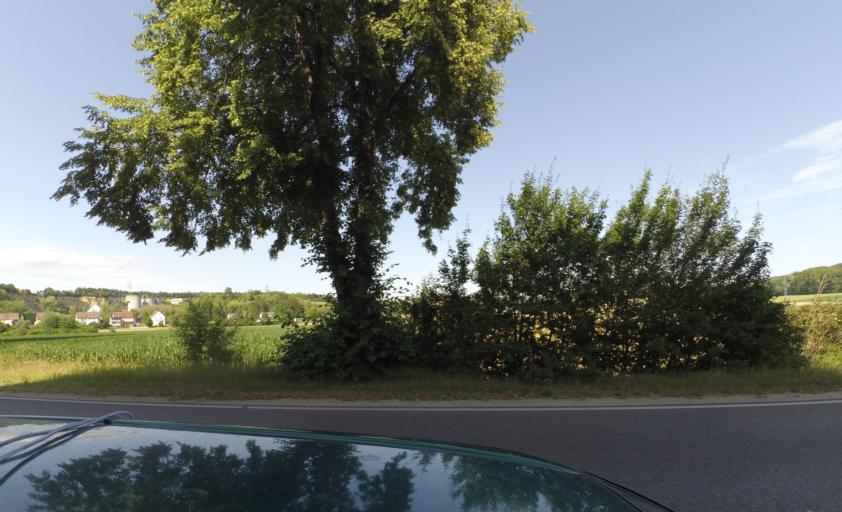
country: DE
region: Baden-Wuerttemberg
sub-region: Regierungsbezirk Stuttgart
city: Bolheim
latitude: 48.6527
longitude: 10.1642
